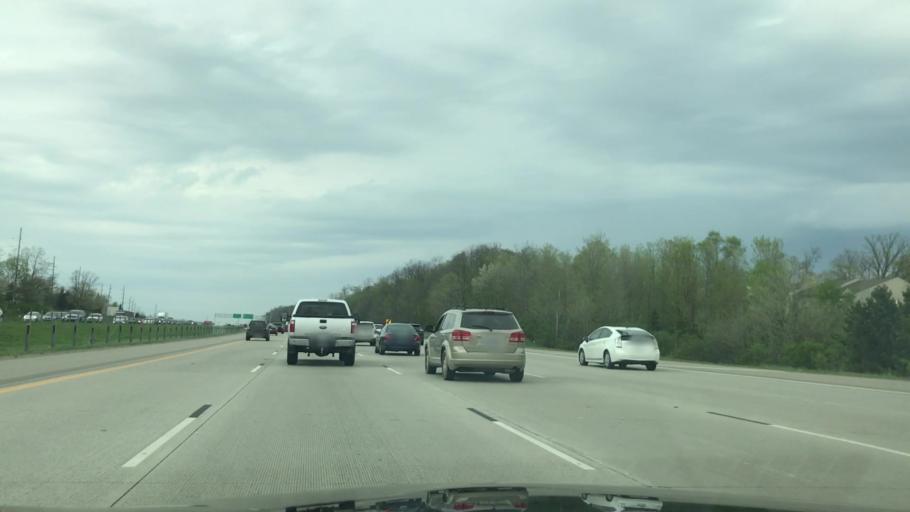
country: US
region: Michigan
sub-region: Wayne County
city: Northville
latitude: 42.4450
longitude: -83.4305
